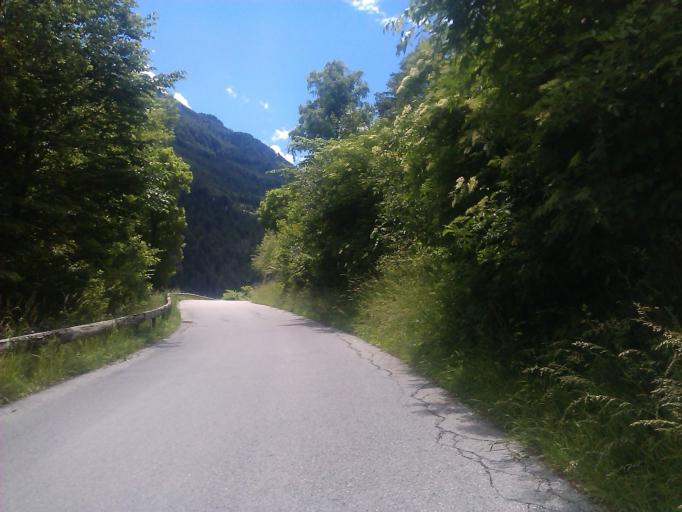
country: AT
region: Tyrol
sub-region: Politischer Bezirk Landeck
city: Serfaus
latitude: 47.0049
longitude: 10.5908
